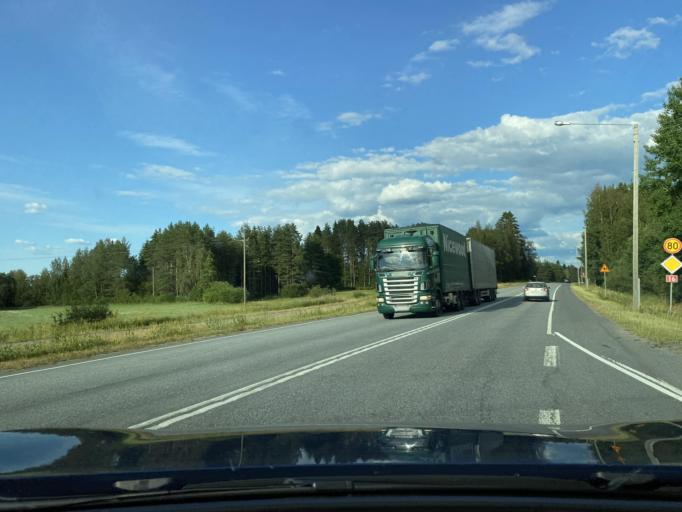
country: FI
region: Southern Ostrobothnia
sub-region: Jaerviseutu
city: Lappajaervi
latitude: 63.0152
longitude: 23.6322
